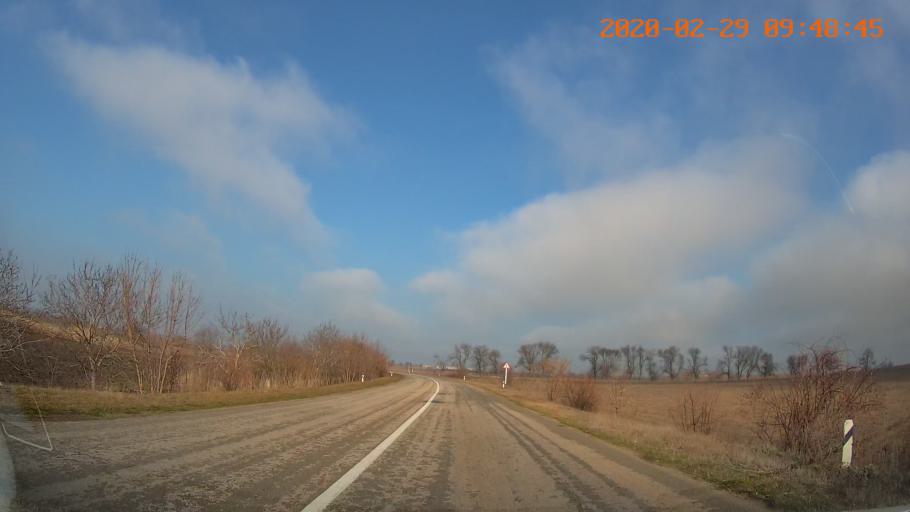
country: MD
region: Telenesti
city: Crasnoe
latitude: 46.6920
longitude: 29.7823
